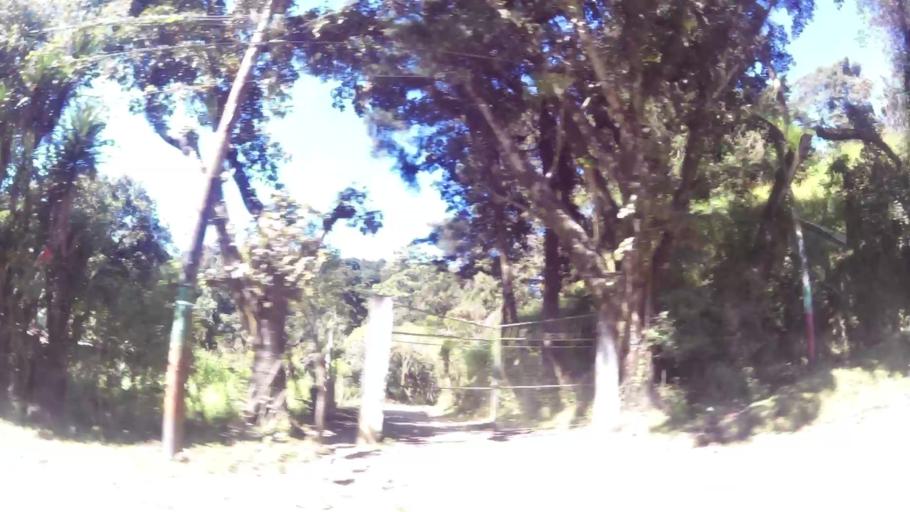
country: GT
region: Guatemala
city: San Jose Pinula
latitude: 14.5310
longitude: -90.4168
